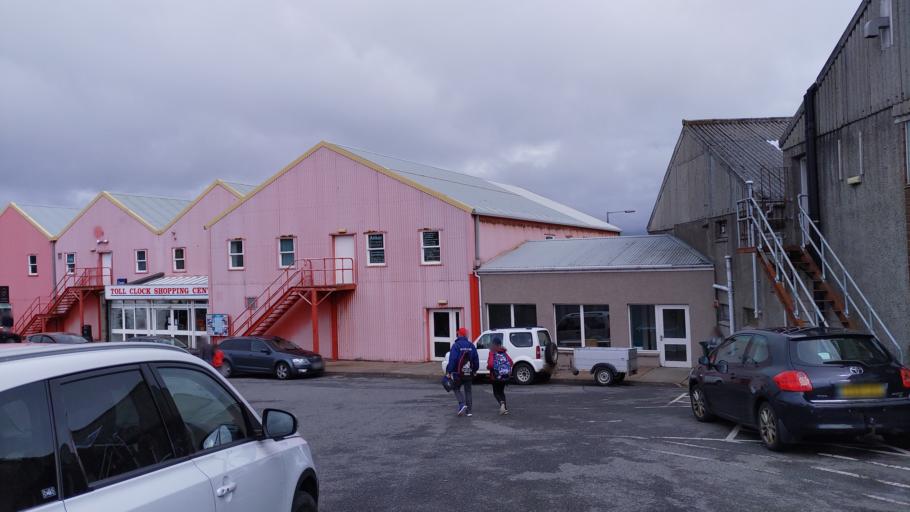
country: GB
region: Scotland
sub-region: Shetland Islands
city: Lerwick
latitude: 60.1578
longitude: -1.1553
